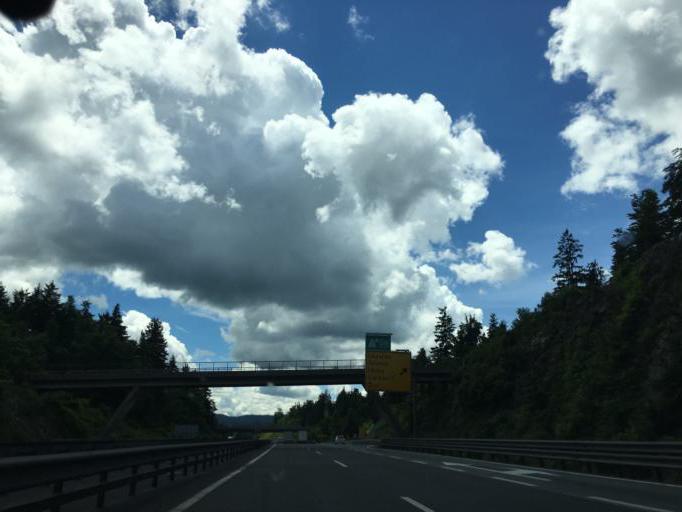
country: SI
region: Logatec
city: Logatec
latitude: 45.9108
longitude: 14.2592
